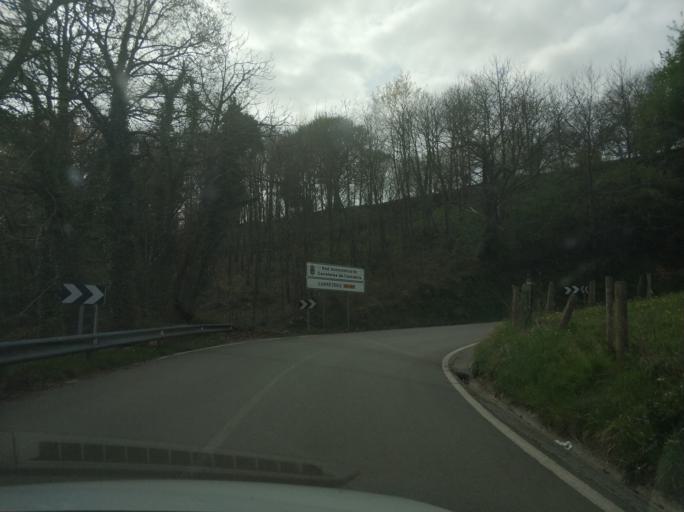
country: ES
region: Cantabria
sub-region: Provincia de Cantabria
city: Ruente
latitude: 43.2392
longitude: -4.2817
